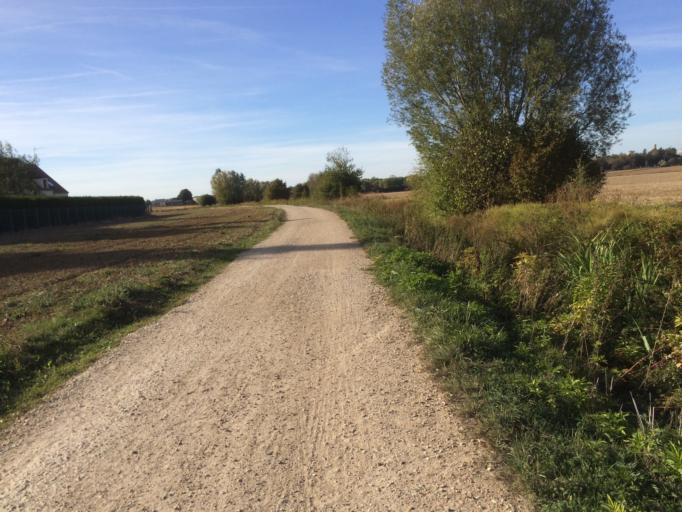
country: FR
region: Ile-de-France
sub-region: Departement de l'Essonne
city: Saclay
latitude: 48.7312
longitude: 2.1822
